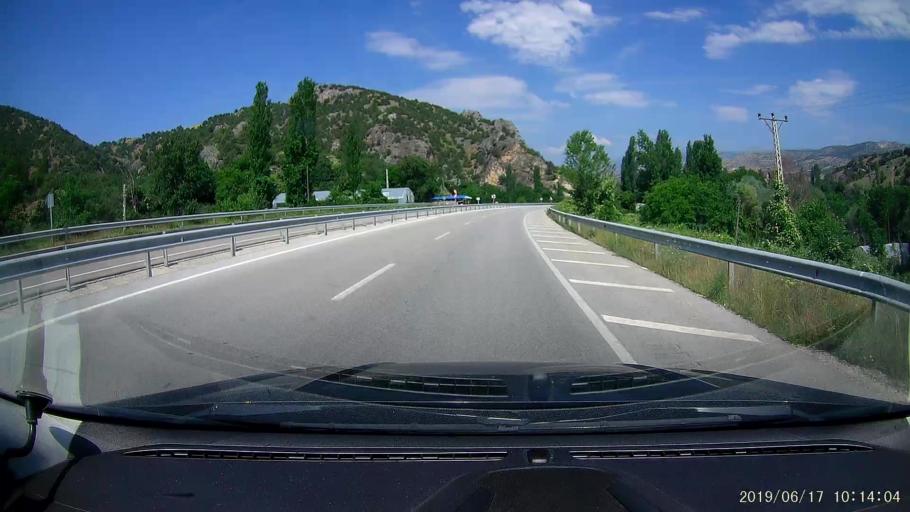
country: TR
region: Amasya
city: Saraycik
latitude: 40.9869
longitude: 35.0335
